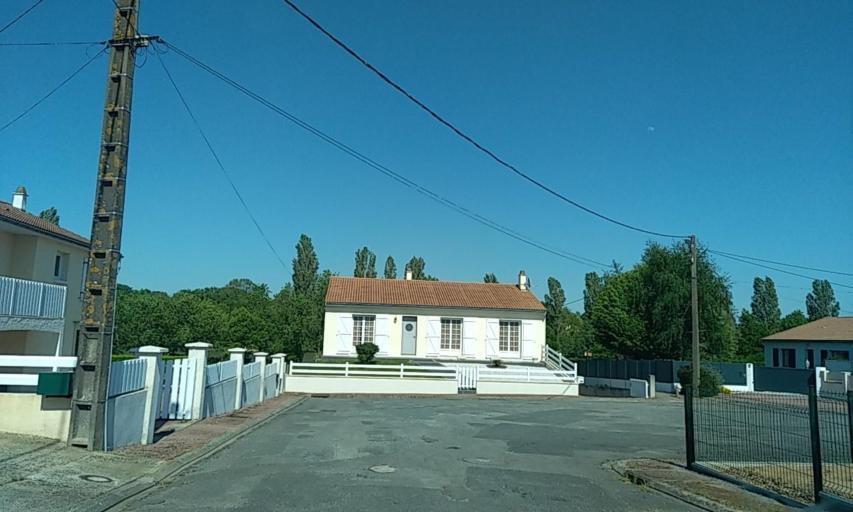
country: FR
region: Poitou-Charentes
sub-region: Departement des Deux-Sevres
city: Boisme
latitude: 46.7763
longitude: -0.4365
